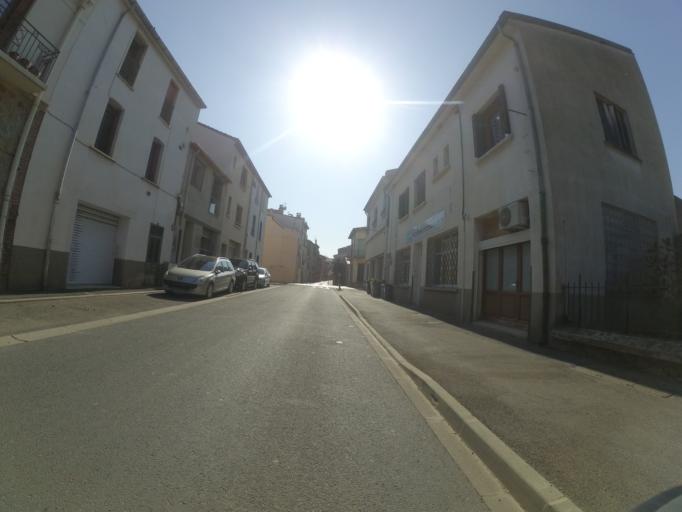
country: FR
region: Languedoc-Roussillon
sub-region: Departement des Pyrenees-Orientales
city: Thuir
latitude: 42.6352
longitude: 2.7533
